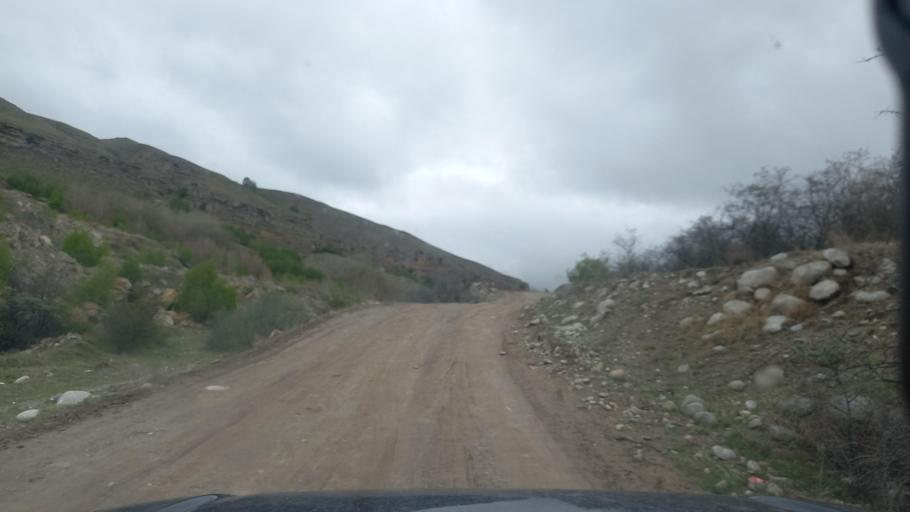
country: RU
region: Kabardino-Balkariya
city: Bylym
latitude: 43.4585
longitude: 42.9962
